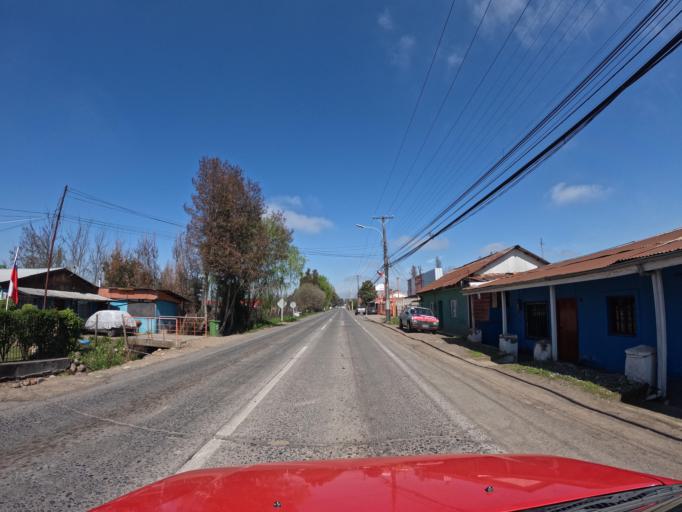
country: CL
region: Maule
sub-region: Provincia de Curico
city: Molina
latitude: -35.0803
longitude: -71.2620
